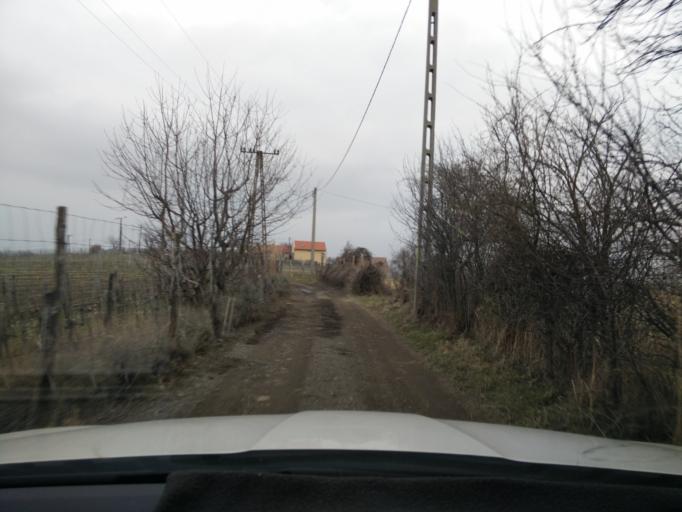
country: HU
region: Tolna
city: Szekszard
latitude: 46.3470
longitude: 18.6700
